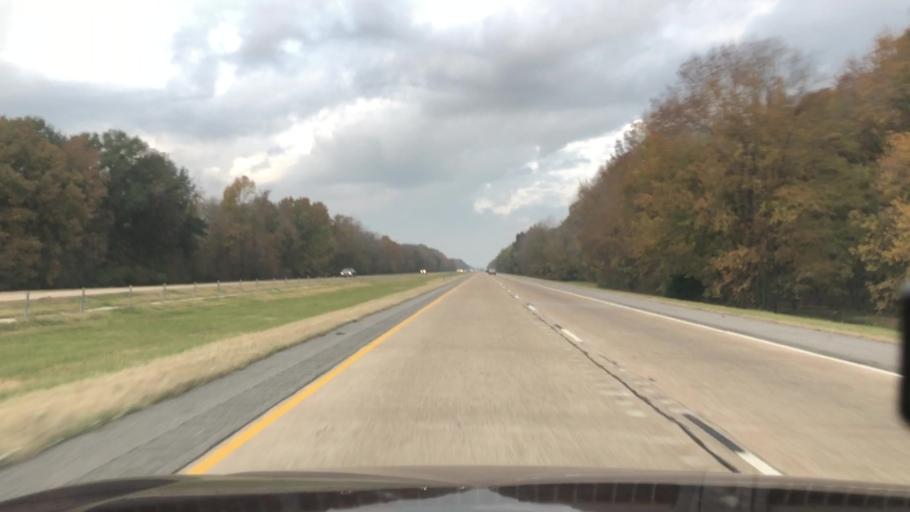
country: US
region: Louisiana
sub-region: Madison Parish
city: Tallulah
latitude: 32.3388
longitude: -91.0671
